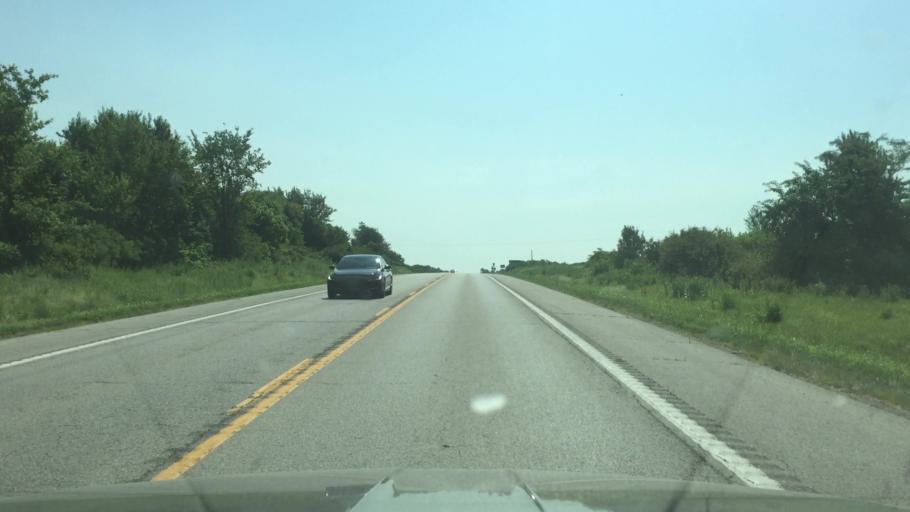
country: US
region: Missouri
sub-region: Pettis County
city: Sedalia
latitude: 38.6939
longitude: -93.1007
